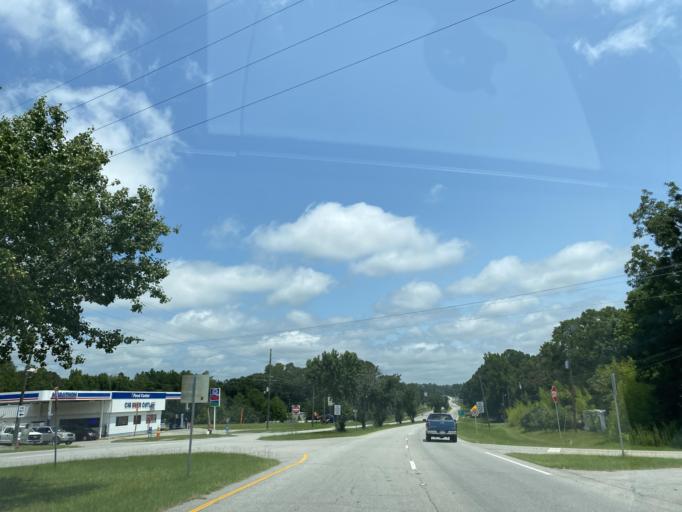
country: US
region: Georgia
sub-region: Telfair County
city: McRae
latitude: 32.0498
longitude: -82.9098
